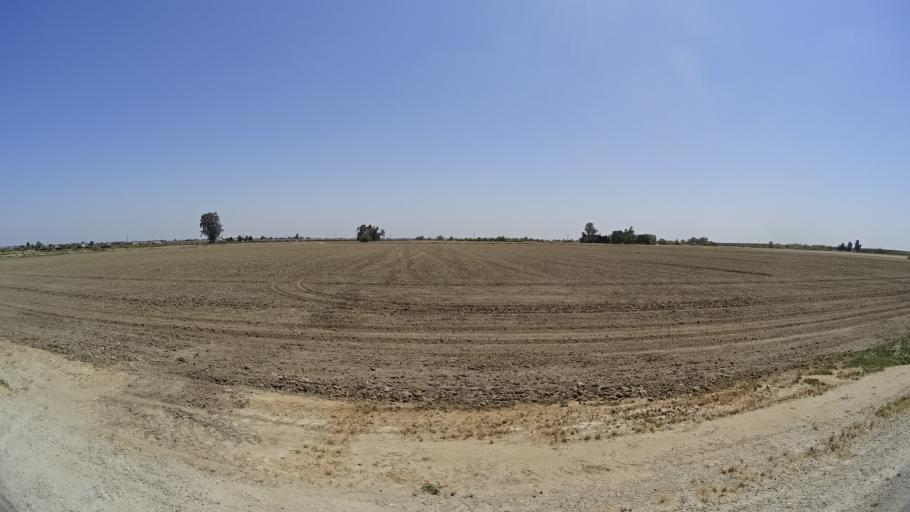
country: US
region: California
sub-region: Kings County
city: Armona
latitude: 36.3043
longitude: -119.6911
